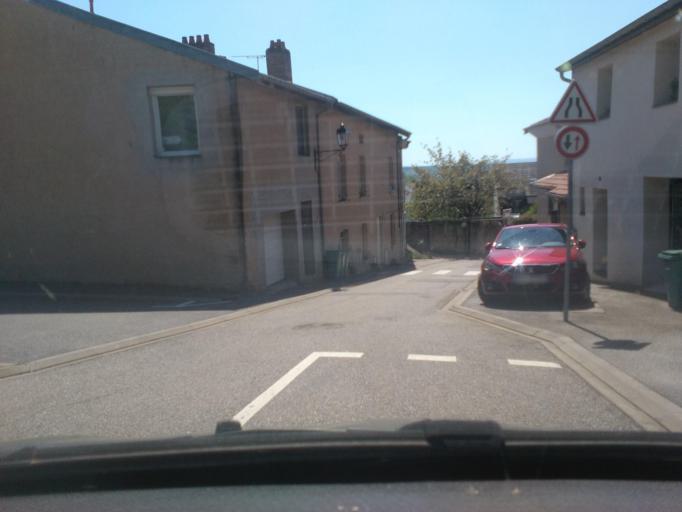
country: FR
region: Lorraine
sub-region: Departement de Meurthe-et-Moselle
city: Ludres
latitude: 48.6240
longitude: 6.1603
